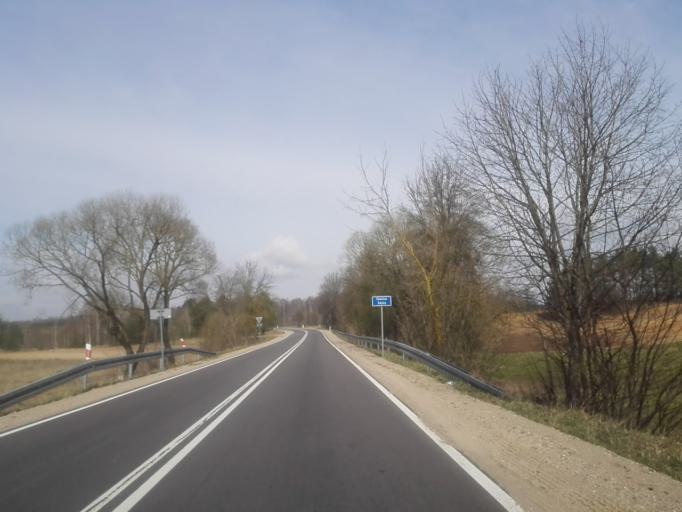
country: PL
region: Podlasie
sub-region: Powiat sejnenski
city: Sejny
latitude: 54.0652
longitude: 23.3585
